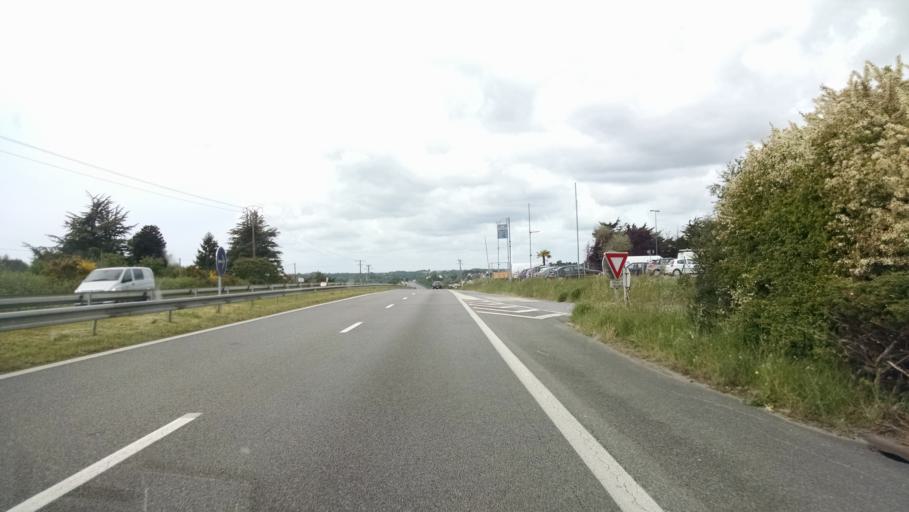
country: FR
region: Brittany
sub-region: Departement du Morbihan
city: Muzillac
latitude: 47.5493
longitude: -2.4589
